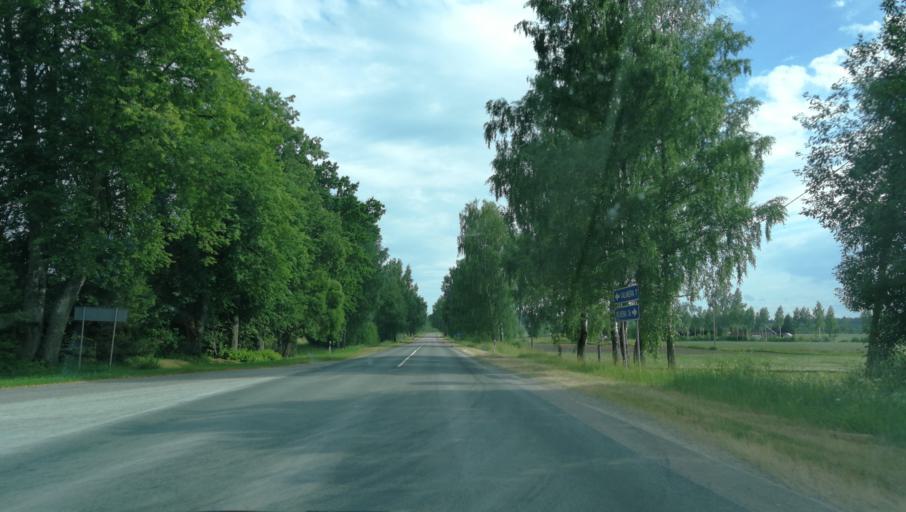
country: LV
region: Valmieras Rajons
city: Valmiera
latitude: 57.5938
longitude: 25.4606
